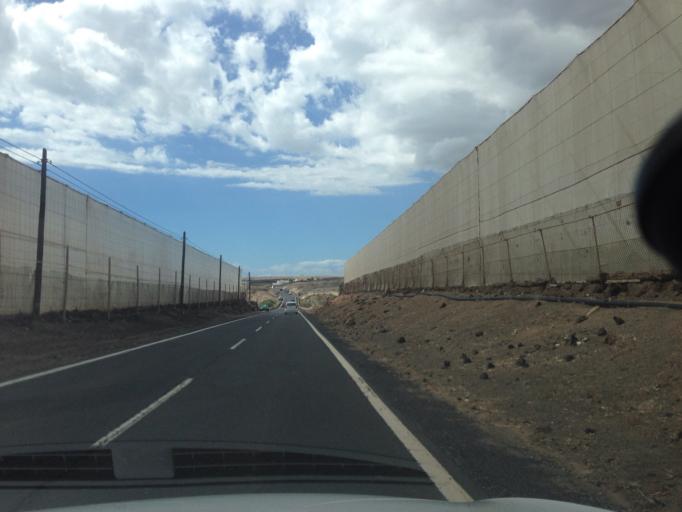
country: ES
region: Canary Islands
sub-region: Provincia de Santa Cruz de Tenerife
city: San Isidro
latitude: 28.0334
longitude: -16.5682
